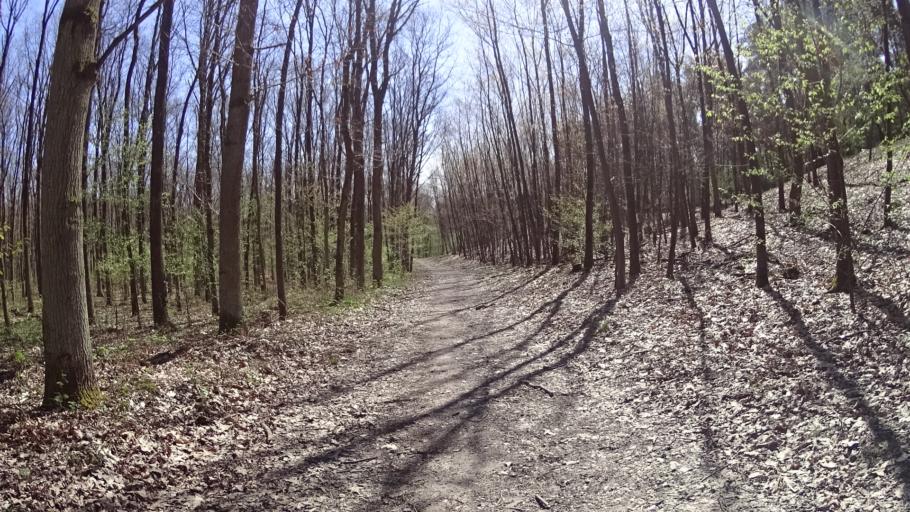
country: DE
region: Hesse
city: Viernheim
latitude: 49.5607
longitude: 8.5892
